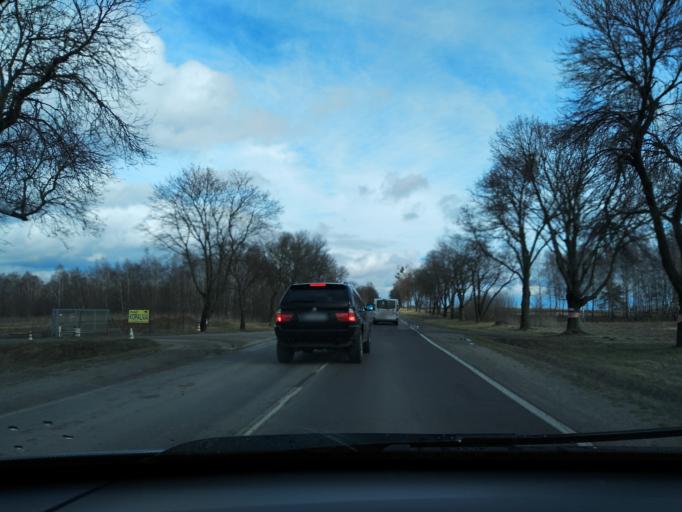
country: PL
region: Lodz Voivodeship
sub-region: Powiat zgierski
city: Strykow
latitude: 51.8664
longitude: 19.5139
